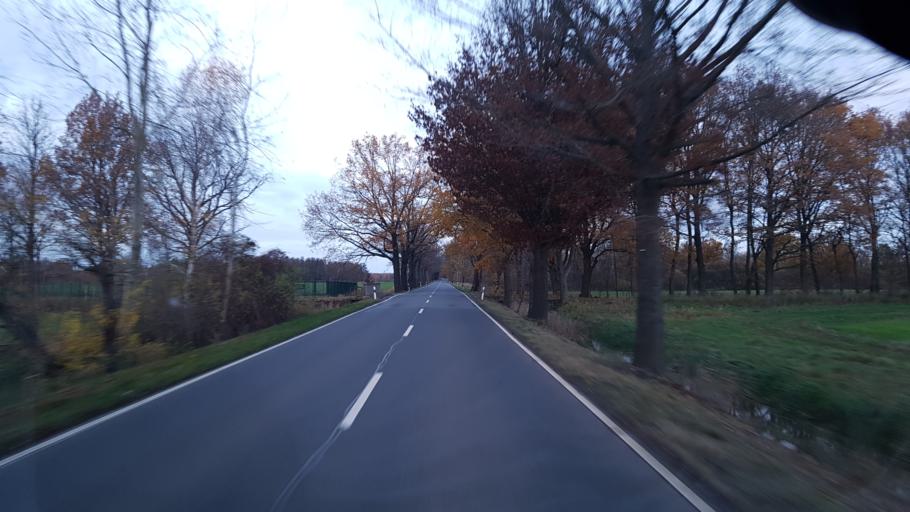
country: DE
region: Brandenburg
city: Schraden
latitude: 51.4532
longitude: 13.7113
